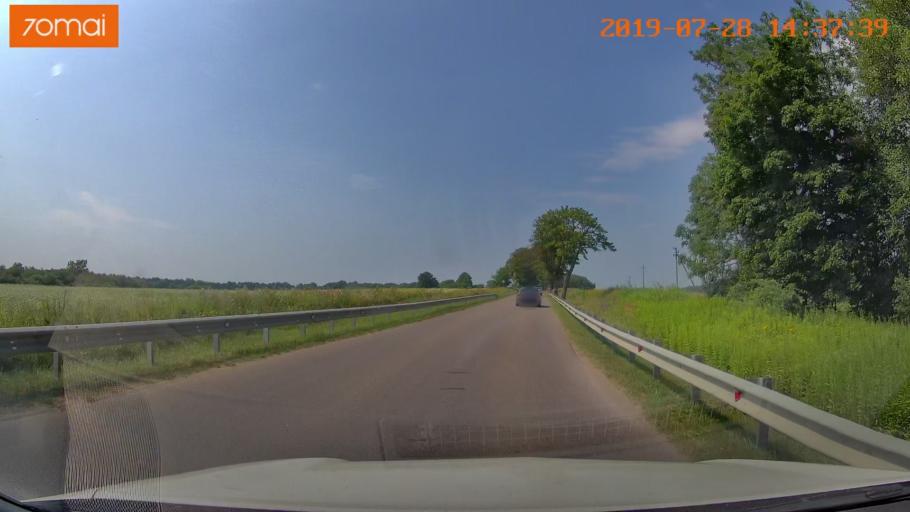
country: RU
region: Kaliningrad
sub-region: Gorod Kaliningrad
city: Yantarnyy
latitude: 54.8410
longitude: 19.9944
